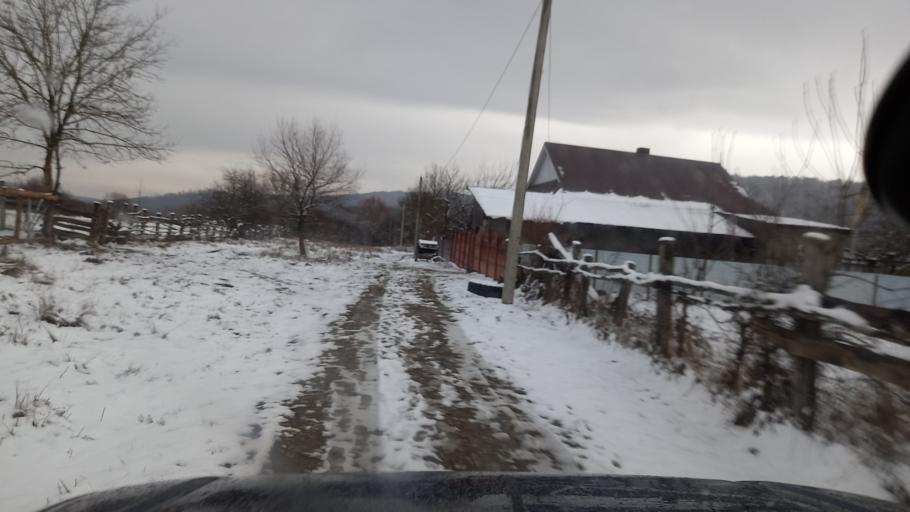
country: RU
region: Adygeya
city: Abadzekhskaya
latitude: 44.3564
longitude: 40.4142
